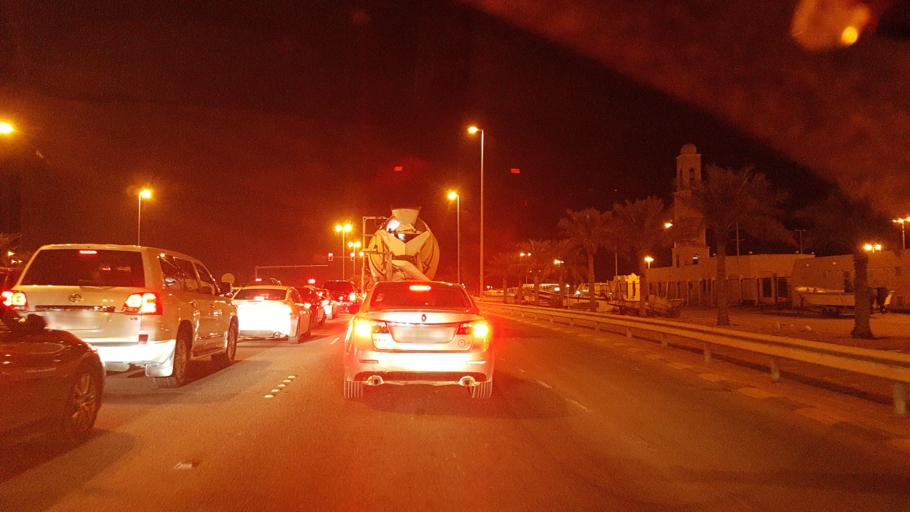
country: BH
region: Muharraq
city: Al Hadd
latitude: 26.2437
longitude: 50.6584
